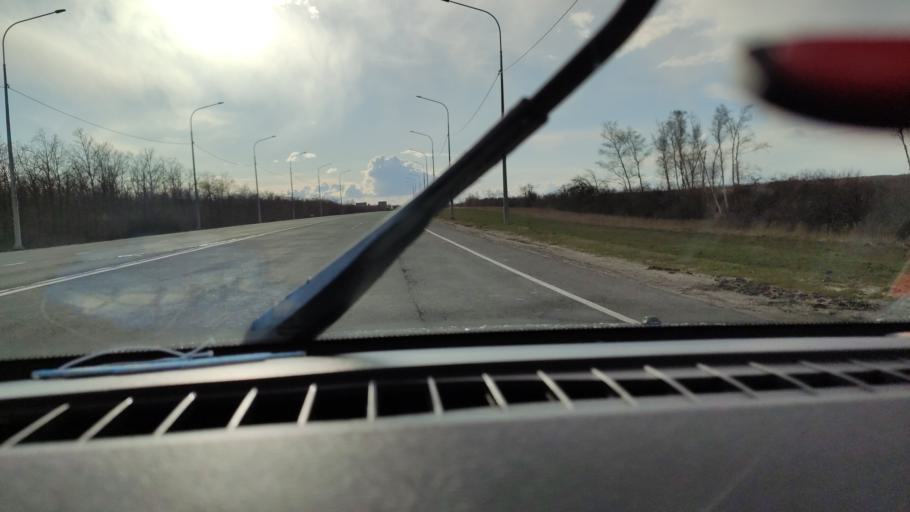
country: RU
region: Saratov
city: Yelshanka
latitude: 51.8203
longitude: 46.3474
